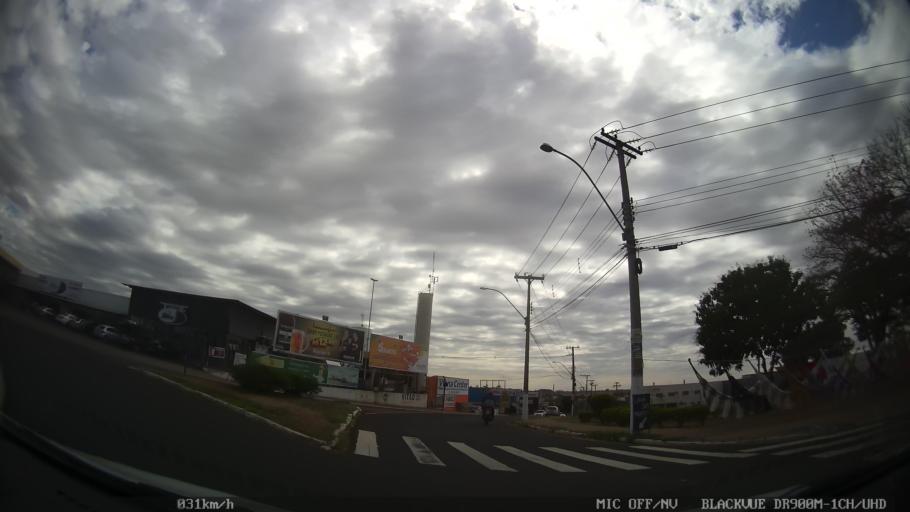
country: BR
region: Sao Paulo
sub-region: Bady Bassitt
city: Bady Bassitt
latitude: -20.8070
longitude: -49.5063
